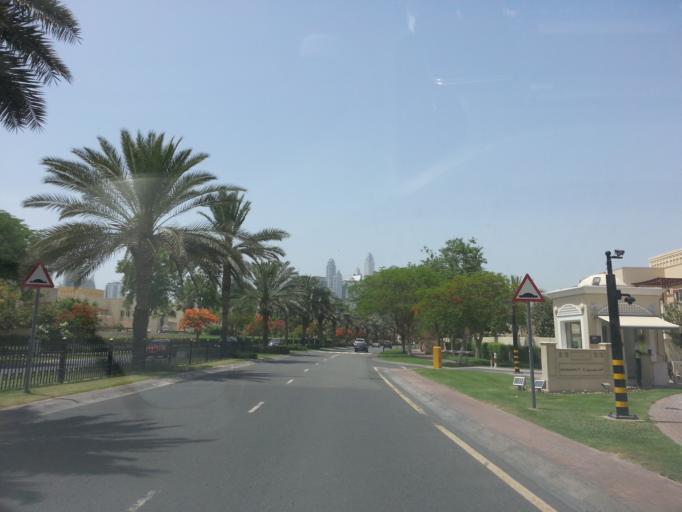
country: AE
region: Dubai
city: Dubai
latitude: 25.0652
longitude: 55.1550
